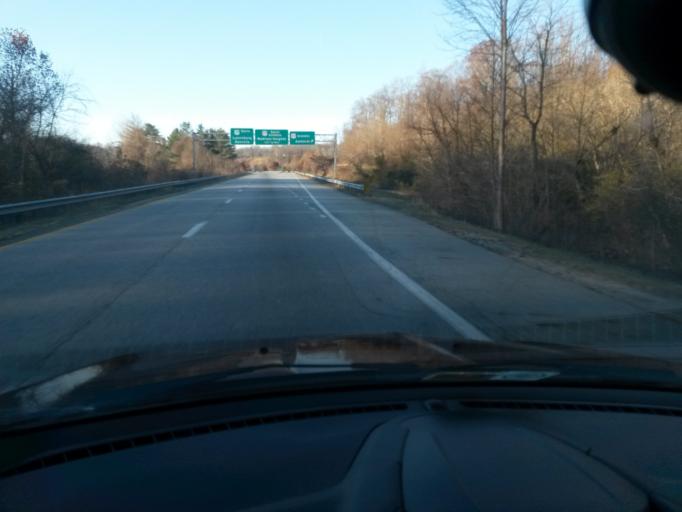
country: US
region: Virginia
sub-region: Amherst County
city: Amherst
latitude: 37.5661
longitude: -79.0587
